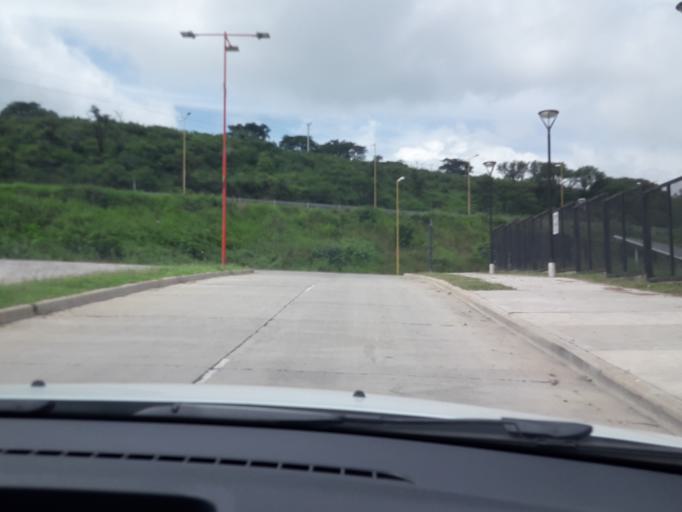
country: AR
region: Jujuy
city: San Salvador de Jujuy
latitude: -24.1849
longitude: -65.3301
